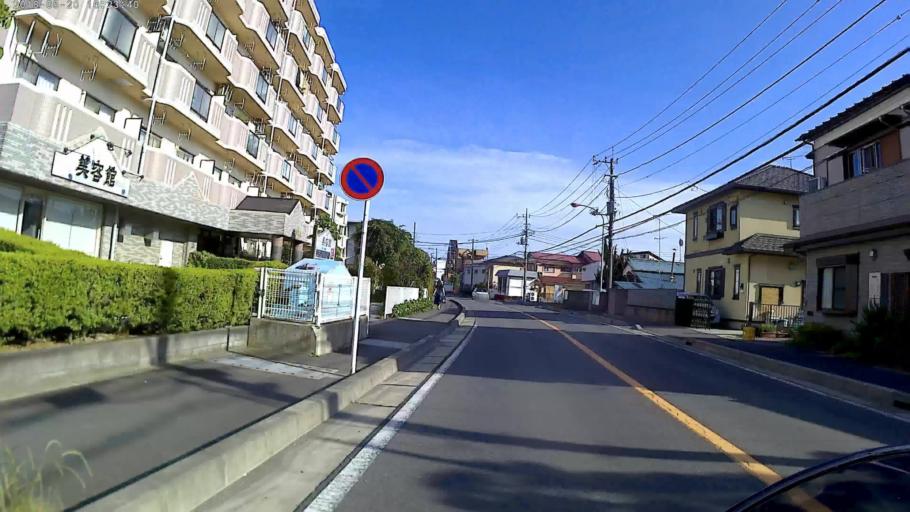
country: JP
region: Kanagawa
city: Odawara
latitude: 35.2914
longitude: 139.1486
